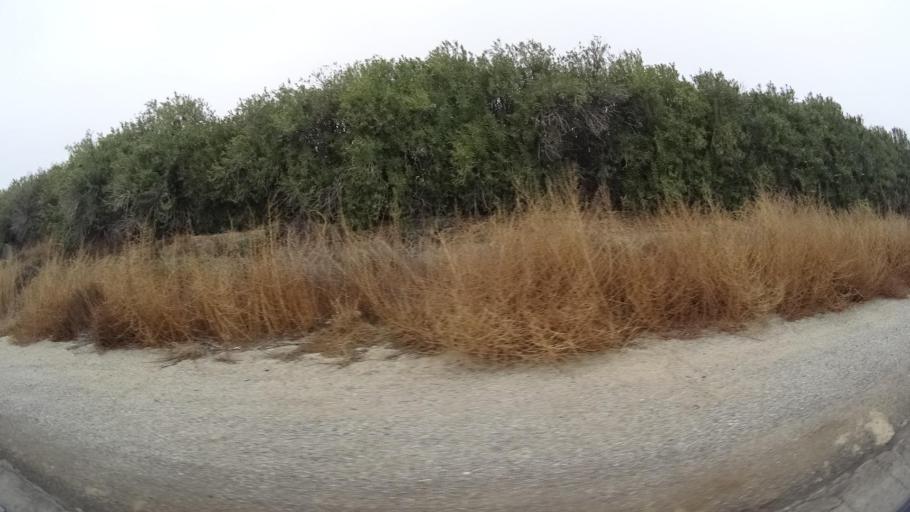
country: US
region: California
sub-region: Kern County
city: Maricopa
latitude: 35.1440
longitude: -119.2395
